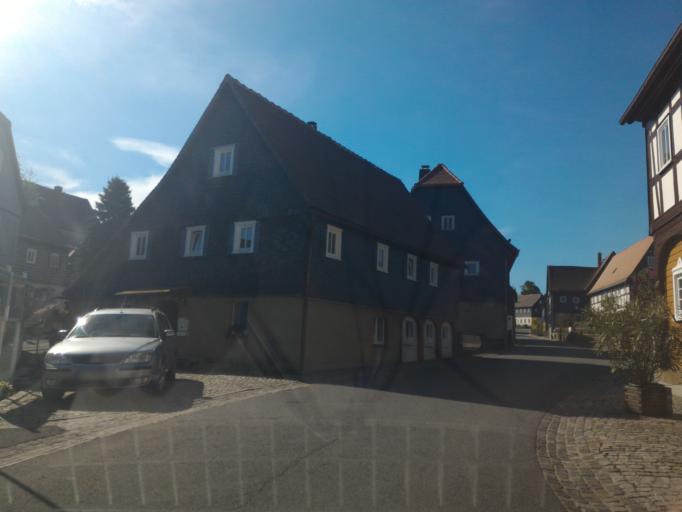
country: DE
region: Saxony
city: Niedercunnersdorf
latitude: 51.0298
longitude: 14.6723
